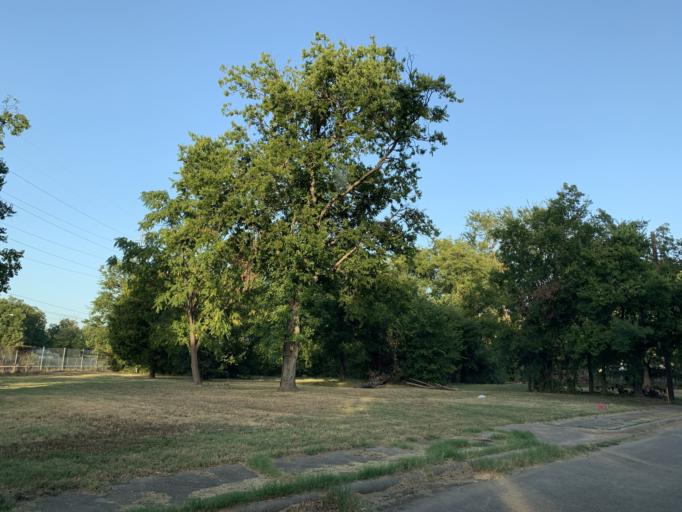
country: US
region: Texas
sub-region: Dallas County
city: Dallas
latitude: 32.7663
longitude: -96.7492
